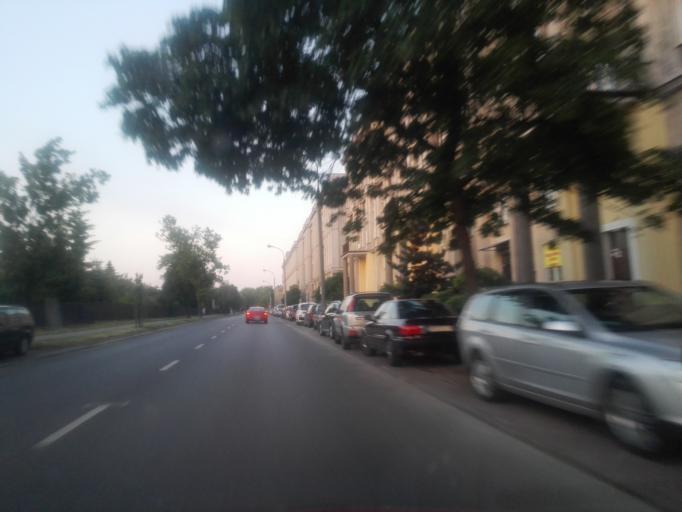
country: PL
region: Masovian Voivodeship
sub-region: Warszawa
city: Mokotow
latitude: 52.1955
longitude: 21.0096
